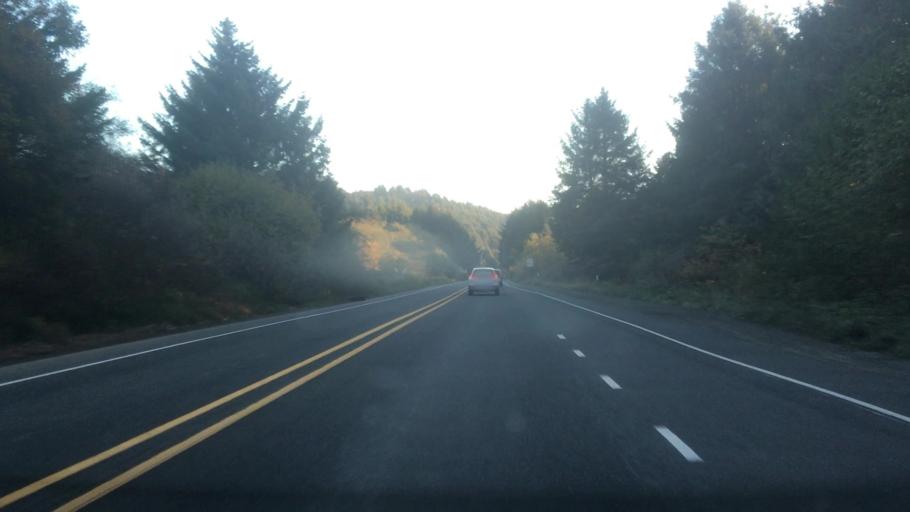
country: US
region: Oregon
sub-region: Clatsop County
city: Cannon Beach
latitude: 45.8701
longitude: -123.9584
